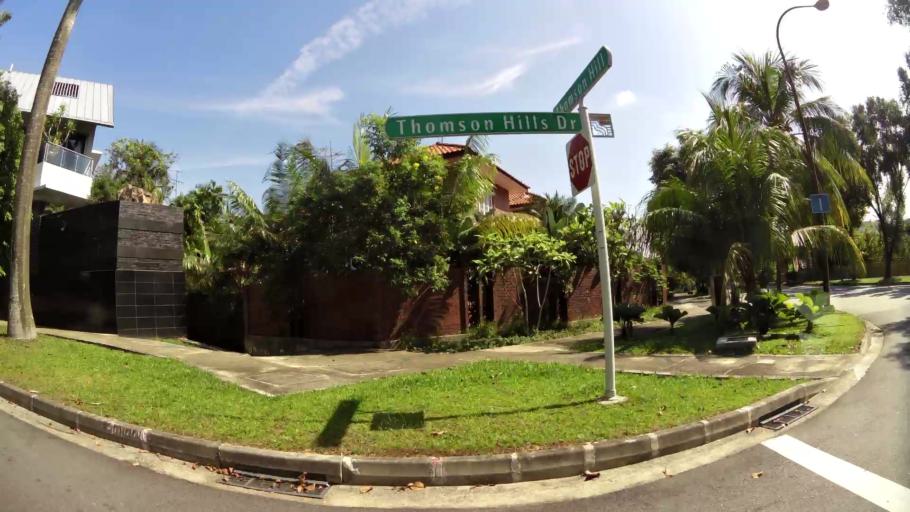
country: SG
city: Singapore
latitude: 1.3776
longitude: 103.8327
